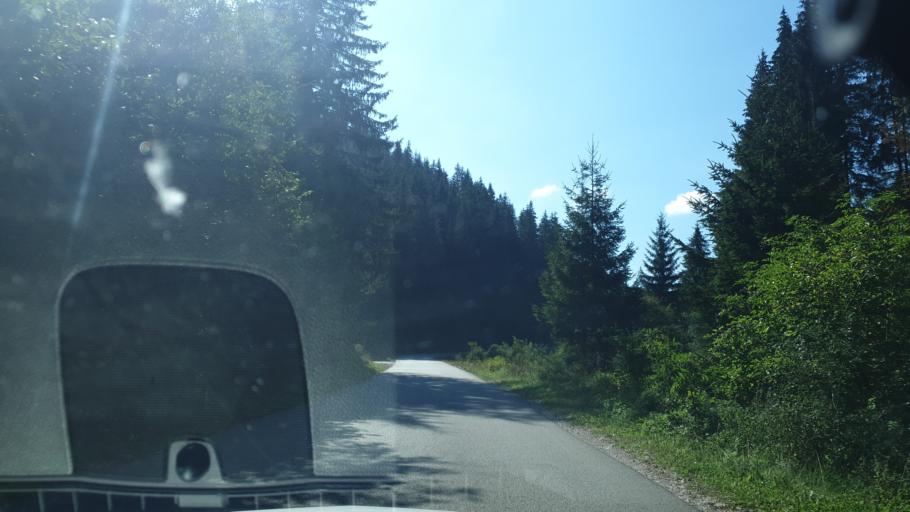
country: RS
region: Central Serbia
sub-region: Zlatiborski Okrug
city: Nova Varos
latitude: 43.4430
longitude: 19.8525
